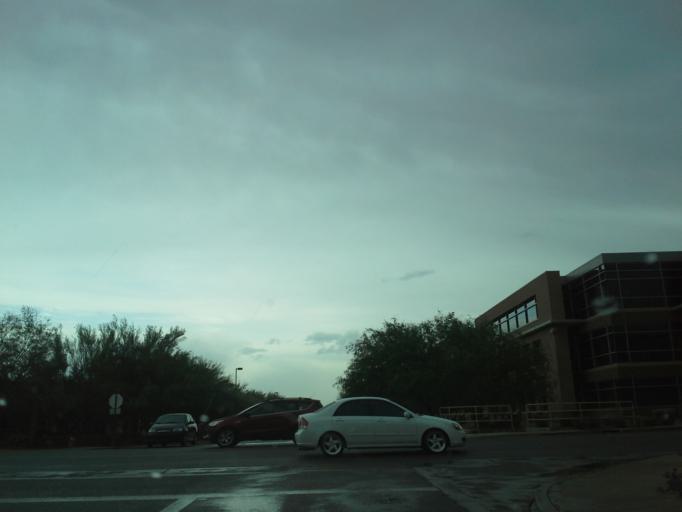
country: US
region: Arizona
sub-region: Maricopa County
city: Paradise Valley
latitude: 33.6372
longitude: -111.8871
